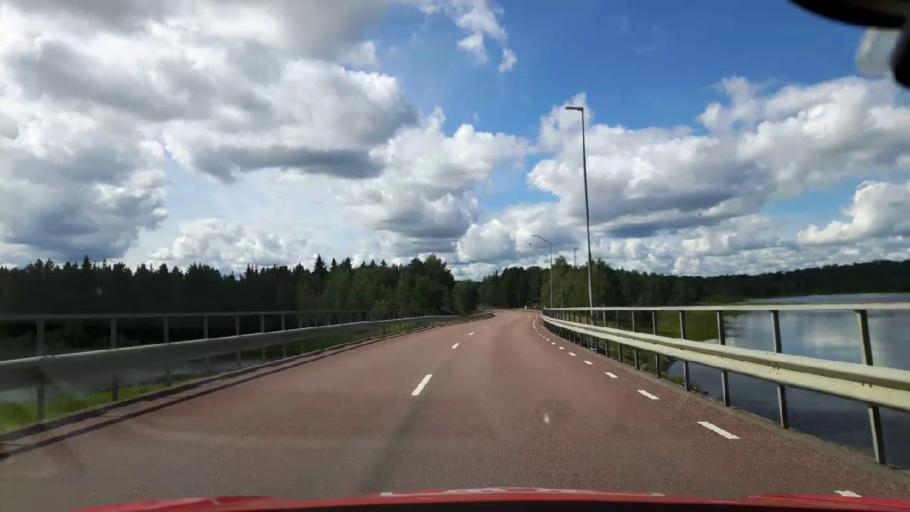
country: SE
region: Jaemtland
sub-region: Harjedalens Kommun
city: Sveg
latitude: 61.8570
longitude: 14.0936
